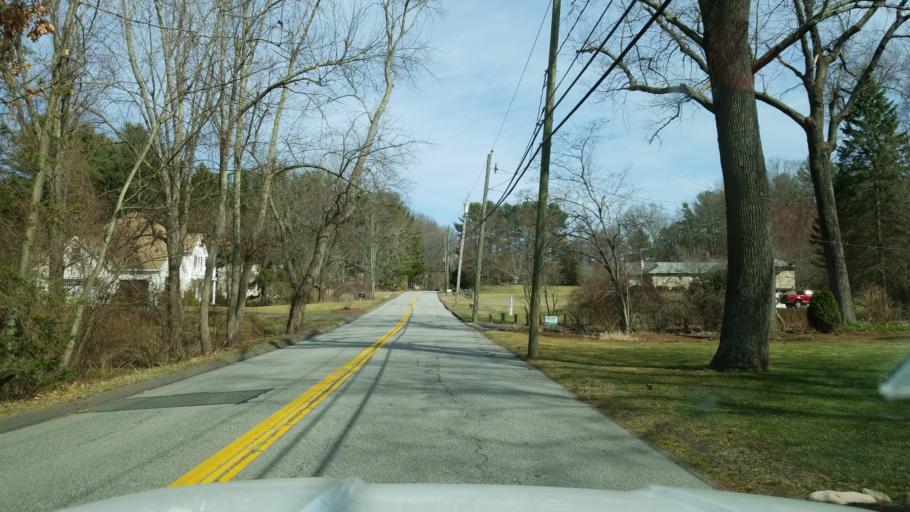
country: US
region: Connecticut
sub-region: Hartford County
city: Glastonbury Center
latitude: 41.7036
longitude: -72.5672
